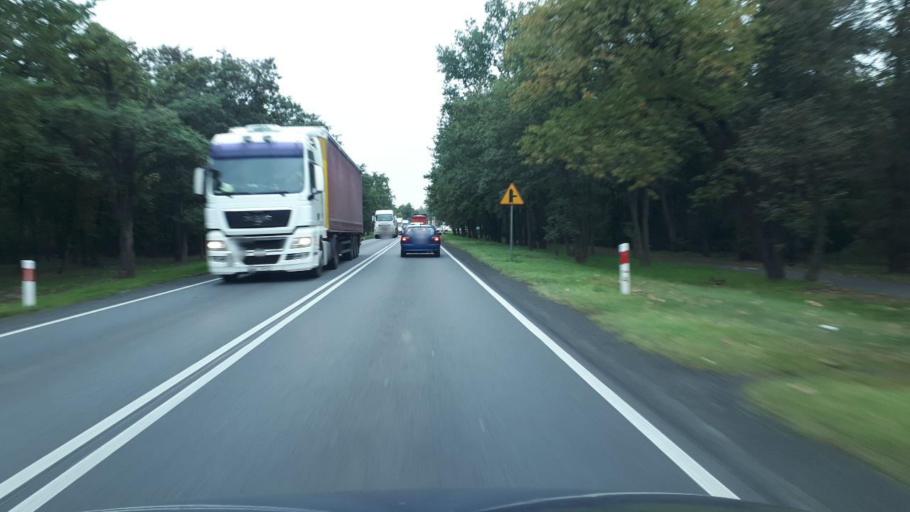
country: PL
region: Greater Poland Voivodeship
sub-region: Powiat ostrzeszowski
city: Ostrzeszow
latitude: 51.4324
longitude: 17.9177
